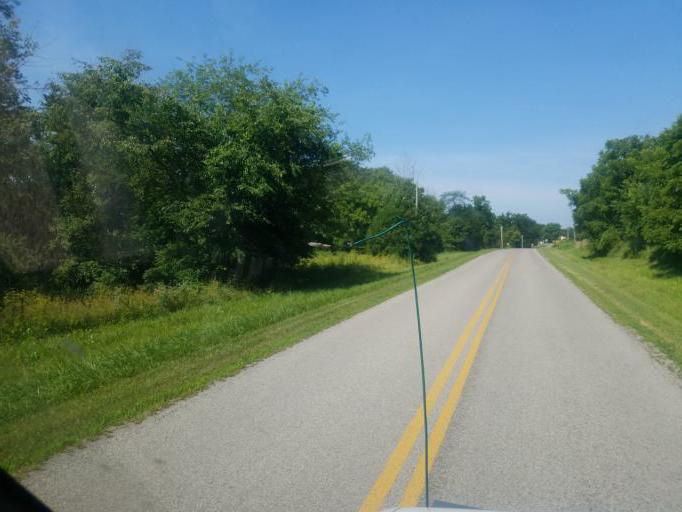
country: US
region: Ohio
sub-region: Union County
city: Marysville
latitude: 40.2823
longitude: -83.2680
